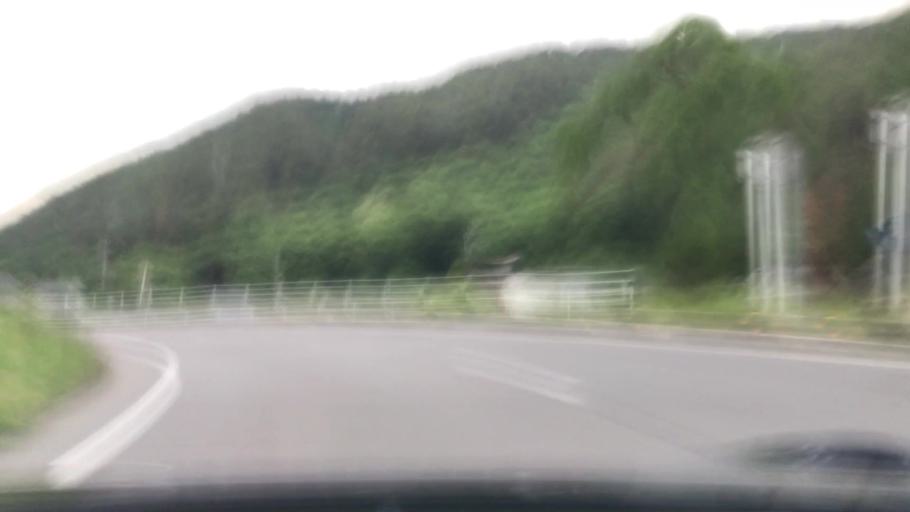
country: JP
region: Nagano
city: Kamimaruko
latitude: 36.2519
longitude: 138.2736
